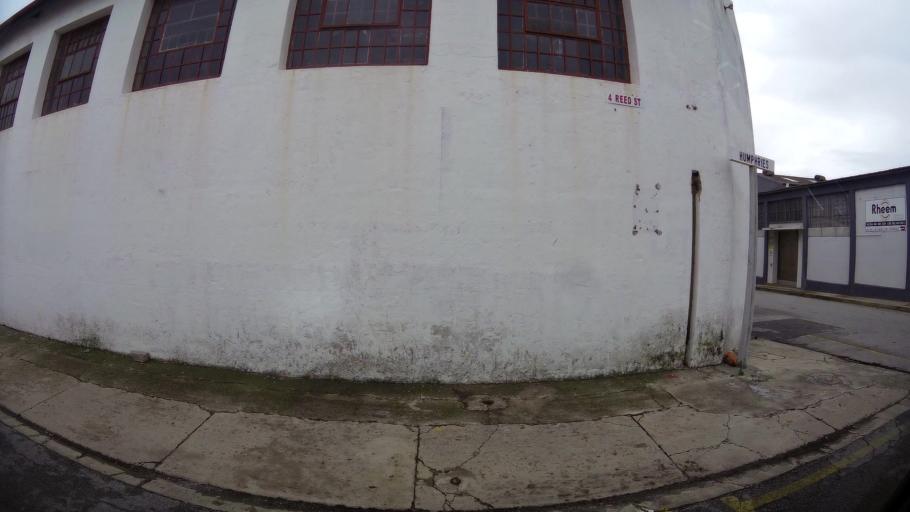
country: ZA
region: Eastern Cape
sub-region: Nelson Mandela Bay Metropolitan Municipality
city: Port Elizabeth
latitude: -33.9514
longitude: 25.6100
